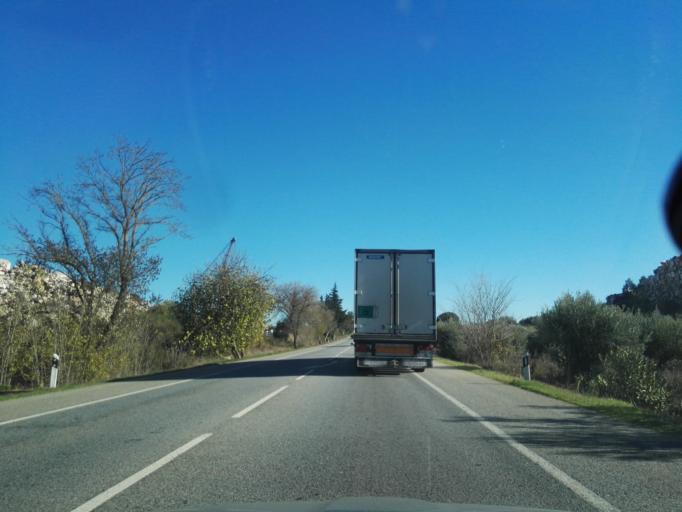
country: PT
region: Evora
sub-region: Estremoz
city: Estremoz
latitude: 38.8359
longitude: -7.5693
